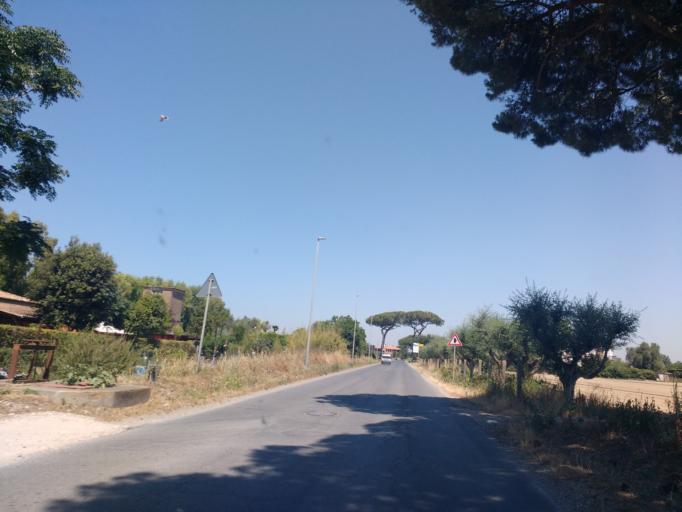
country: IT
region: Latium
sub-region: Citta metropolitana di Roma Capitale
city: Fregene
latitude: 41.8480
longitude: 12.2202
